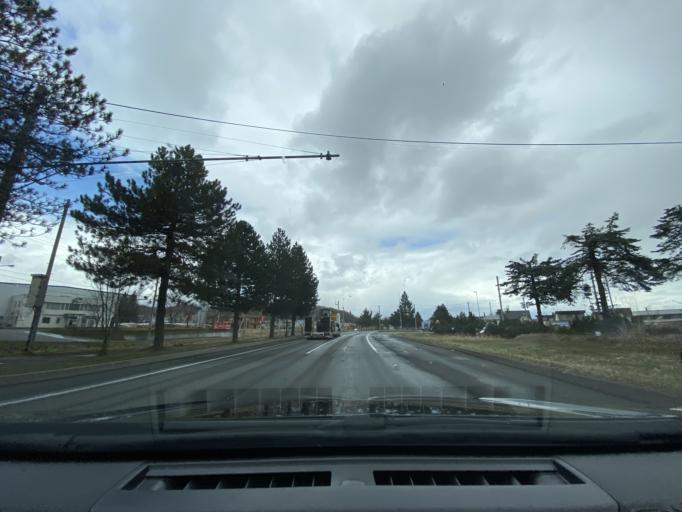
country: JP
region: Hokkaido
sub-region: Asahikawa-shi
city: Asahikawa
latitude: 43.7772
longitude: 142.3067
